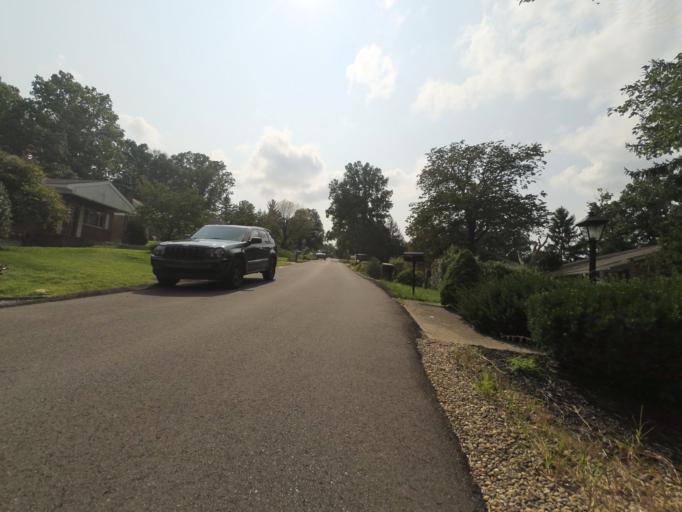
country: US
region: West Virginia
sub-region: Cabell County
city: Huntington
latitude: 38.3980
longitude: -82.4035
